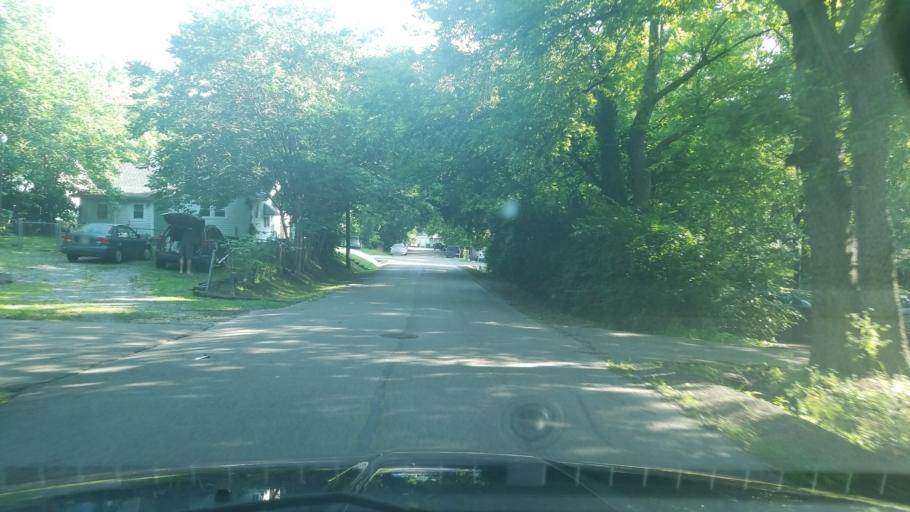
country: US
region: Tennessee
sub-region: Davidson County
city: Oak Hill
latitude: 36.1056
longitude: -86.7447
